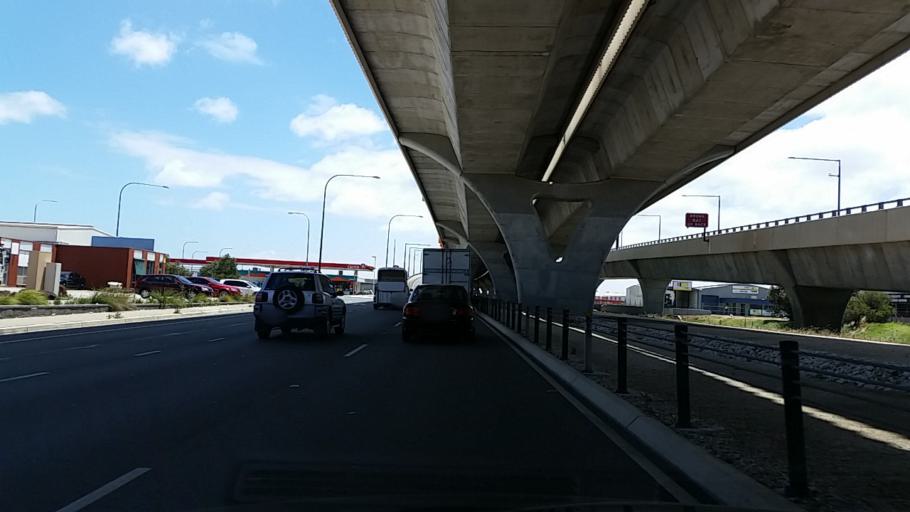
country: AU
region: South Australia
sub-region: Charles Sturt
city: Woodville North
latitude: -34.8483
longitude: 138.5644
